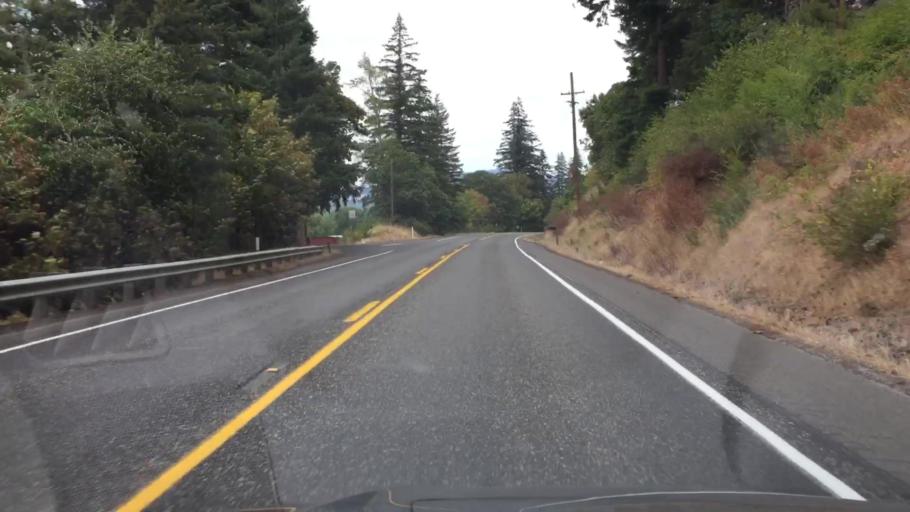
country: US
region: Washington
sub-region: Klickitat County
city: White Salmon
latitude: 45.7816
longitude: -121.5068
